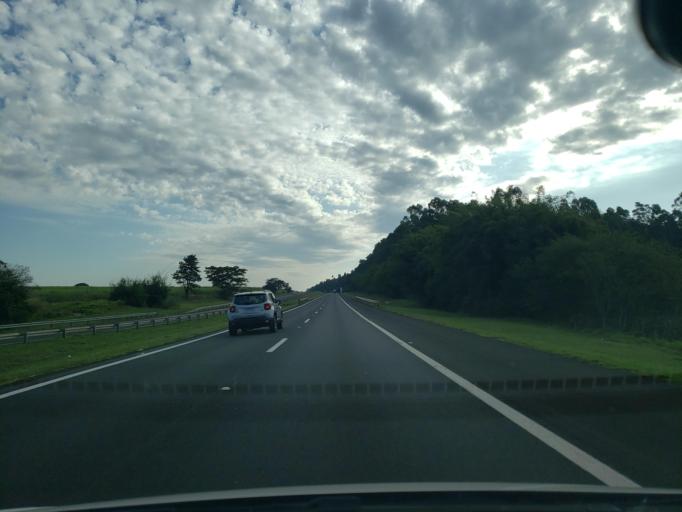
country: BR
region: Sao Paulo
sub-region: Guararapes
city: Guararapes
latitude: -21.2002
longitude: -50.5595
